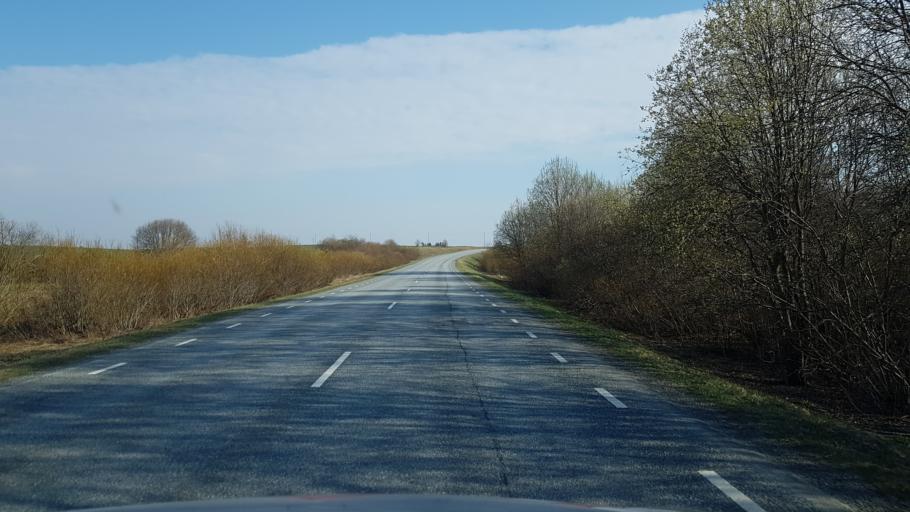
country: EE
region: Laeaene-Virumaa
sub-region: Kadrina vald
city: Kadrina
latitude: 59.3673
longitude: 26.1055
